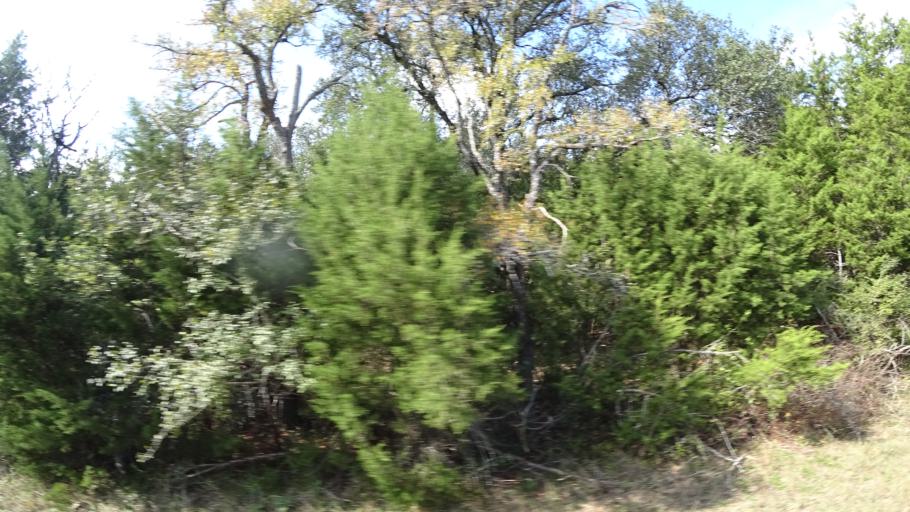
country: US
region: Texas
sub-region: Travis County
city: Wells Branch
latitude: 30.4364
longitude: -97.7088
